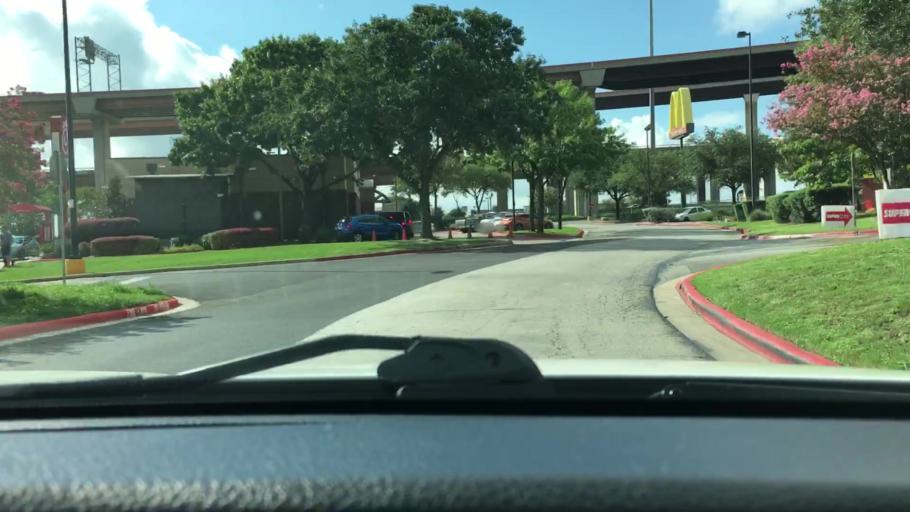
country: US
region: Texas
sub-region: Williamson County
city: Round Rock
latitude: 30.4821
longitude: -97.6722
